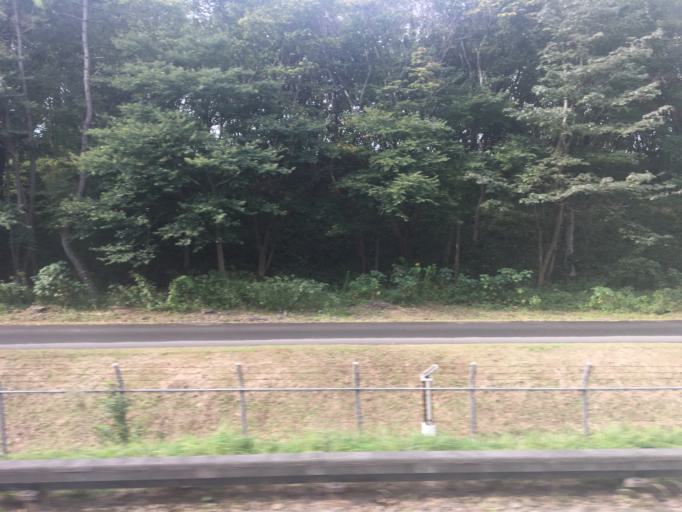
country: JP
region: Saitama
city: Sayama
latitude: 35.8417
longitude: 139.4205
